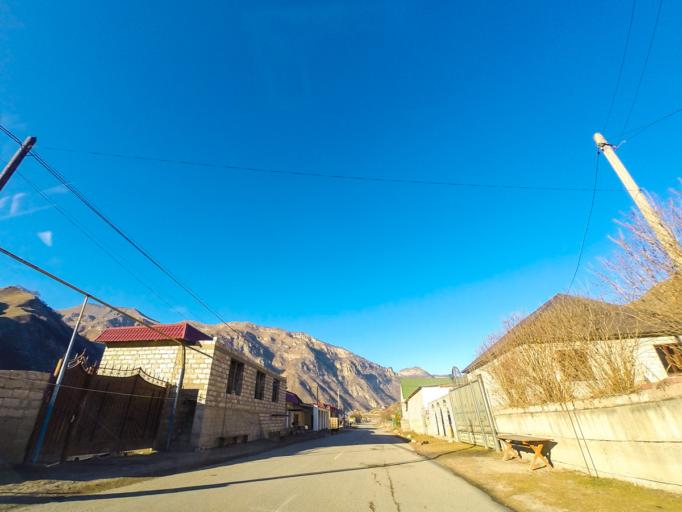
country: RU
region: Kabardino-Balkariya
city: Zhankhoteko
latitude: 43.4264
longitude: 43.2322
